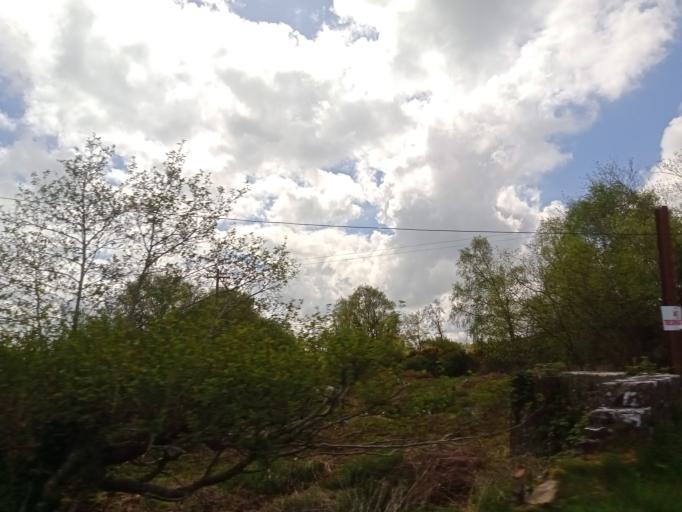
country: IE
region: Munster
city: Thurles
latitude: 52.6903
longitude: -7.6470
